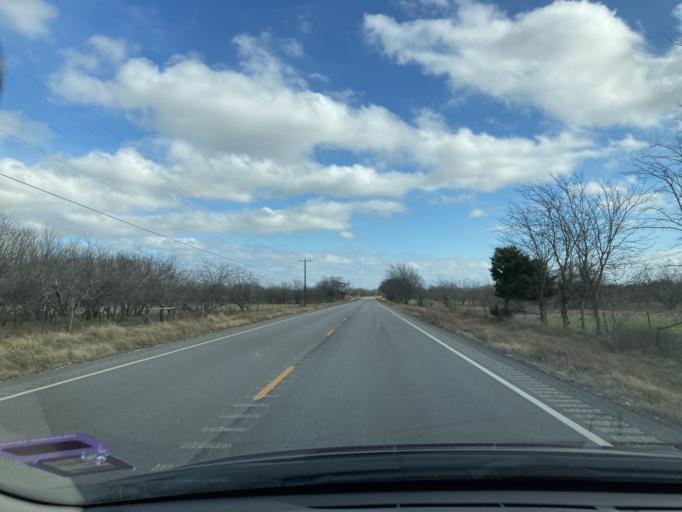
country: US
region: Texas
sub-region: Navarro County
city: Corsicana
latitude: 32.0546
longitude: -96.3604
